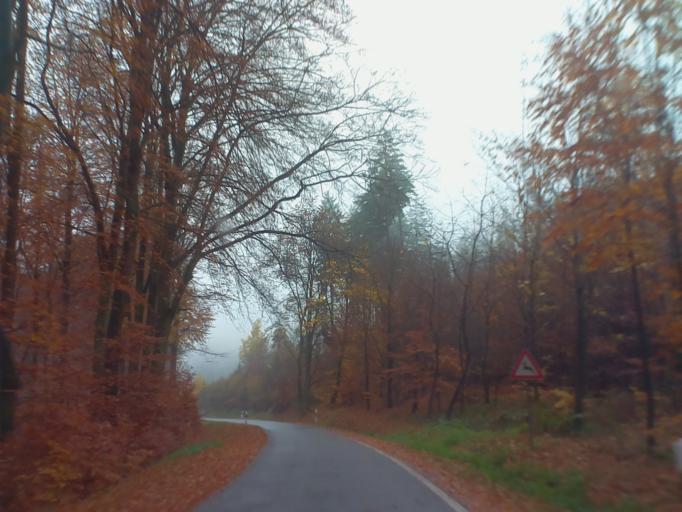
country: DE
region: Hesse
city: Neckarsteinach
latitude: 49.4306
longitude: 8.8521
